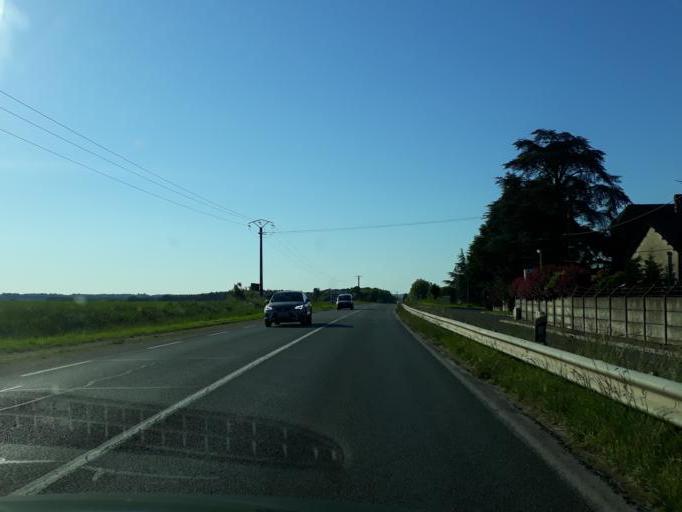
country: FR
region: Centre
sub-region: Departement du Loiret
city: Briare
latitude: 47.6113
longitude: 2.7720
